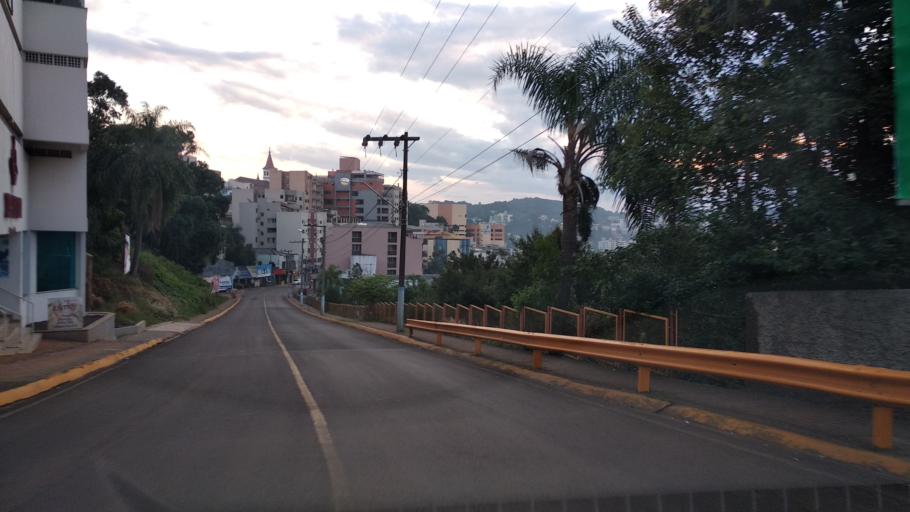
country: BR
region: Santa Catarina
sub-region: Videira
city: Videira
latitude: -27.0053
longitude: -51.1468
